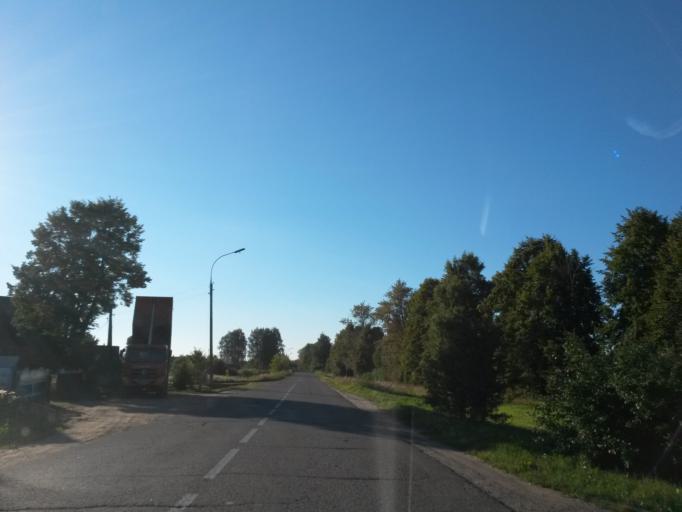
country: RU
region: Jaroslavl
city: Gavrilov-Yam
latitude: 57.2920
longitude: 39.8833
